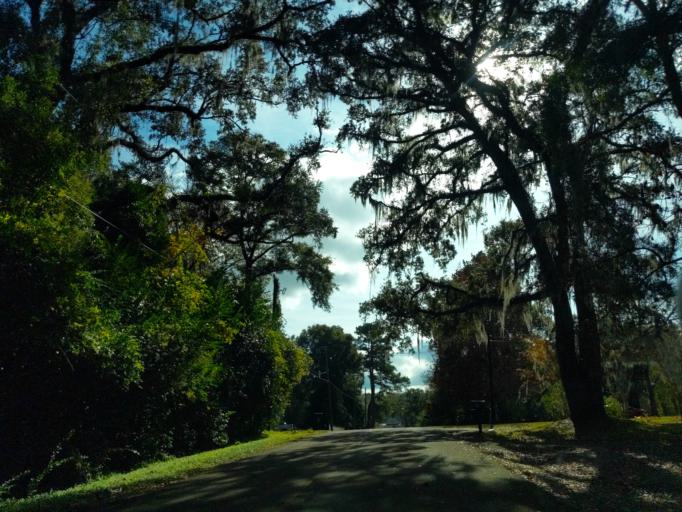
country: US
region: Florida
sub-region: Leon County
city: Tallahassee
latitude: 30.4712
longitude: -84.2022
